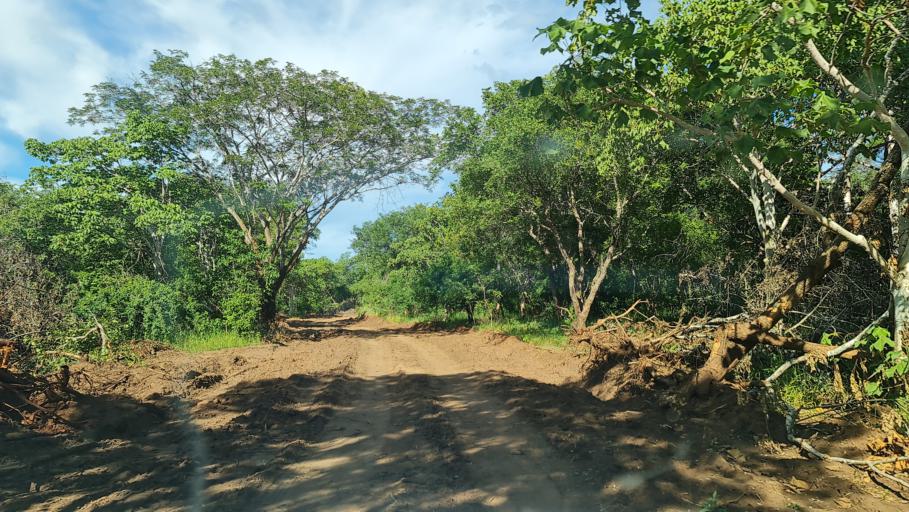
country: MZ
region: Nampula
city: Antonio Enes
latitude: -15.5097
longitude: 40.1356
